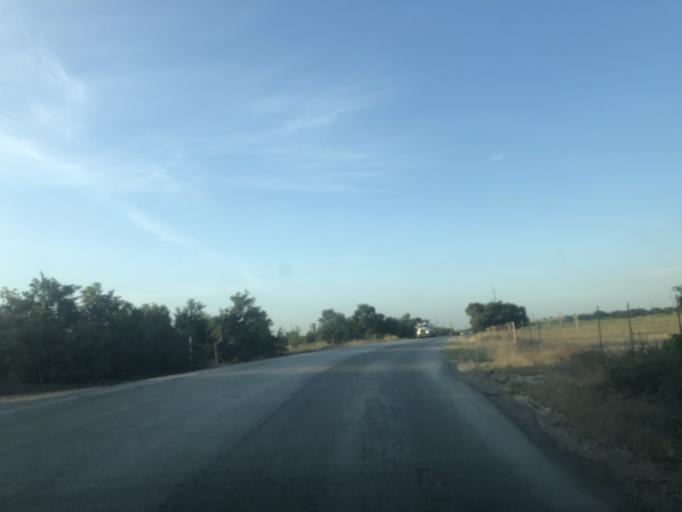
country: US
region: Texas
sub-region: Tarrant County
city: Lakeside
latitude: 32.7864
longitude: -97.4869
